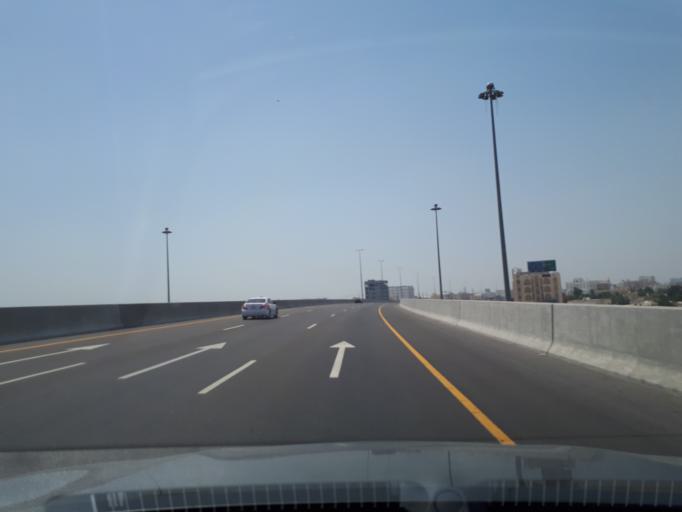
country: OM
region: Al Batinah
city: Al Liwa'
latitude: 24.4239
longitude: 56.6120
